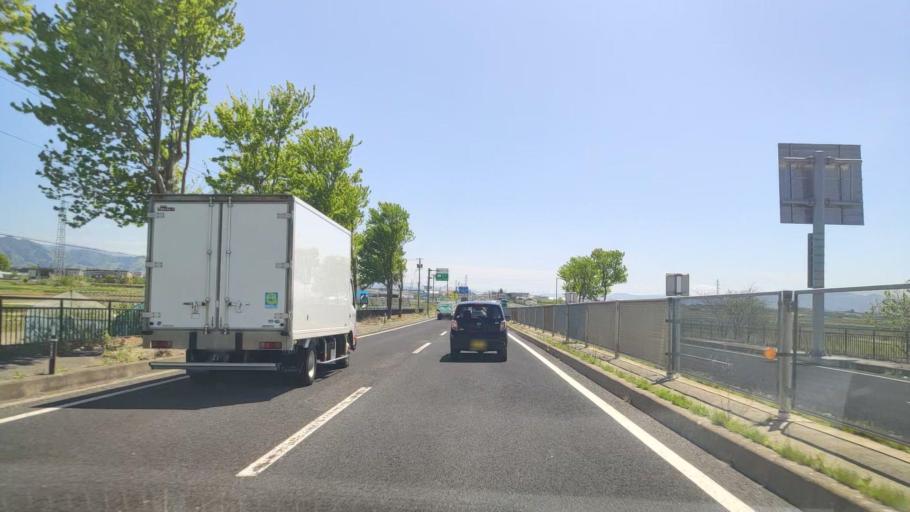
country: JP
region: Yamagata
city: Higashine
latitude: 38.4451
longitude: 140.3810
